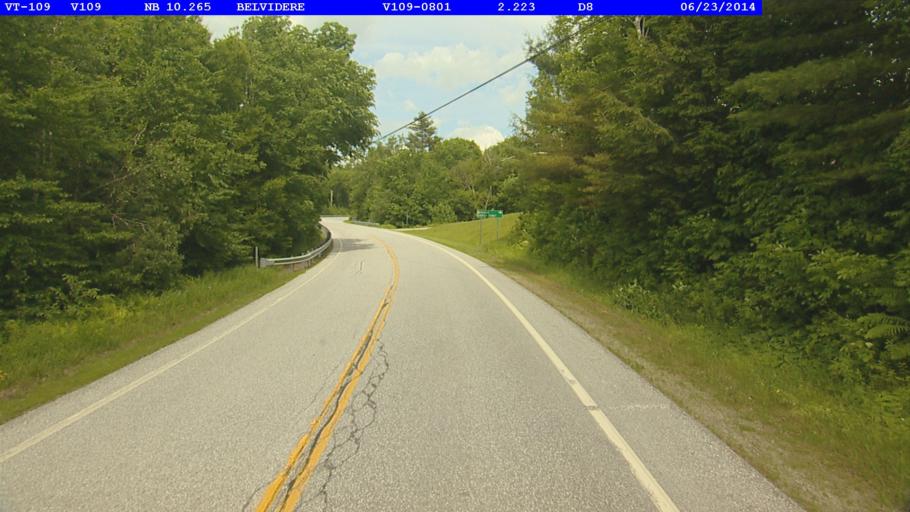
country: US
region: Vermont
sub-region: Lamoille County
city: Johnson
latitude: 44.7472
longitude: -72.7026
